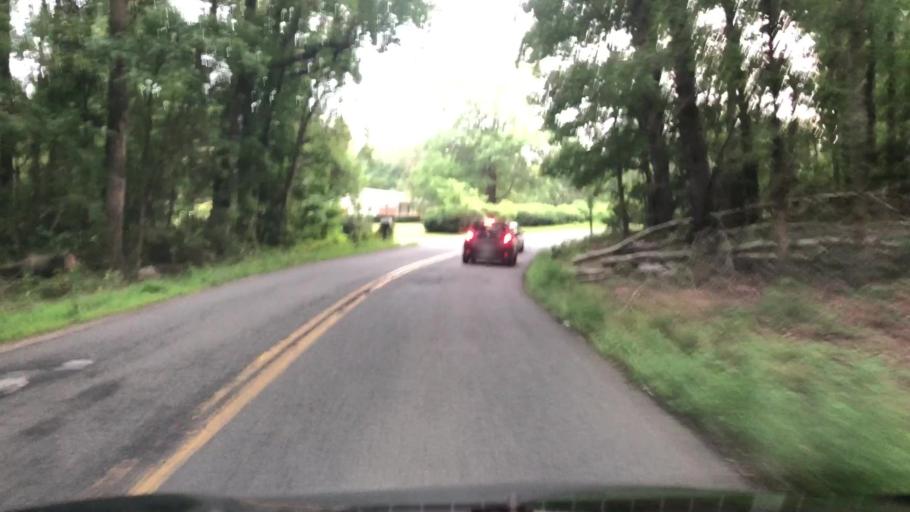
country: US
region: Virginia
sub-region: Fauquier County
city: Bealeton
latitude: 38.5044
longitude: -77.6833
